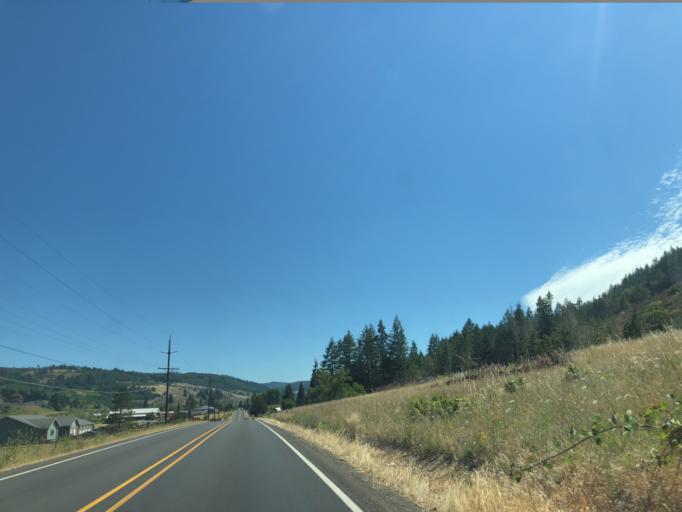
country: US
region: Oregon
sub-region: Douglas County
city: Yoncalla
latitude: 43.5765
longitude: -123.2808
